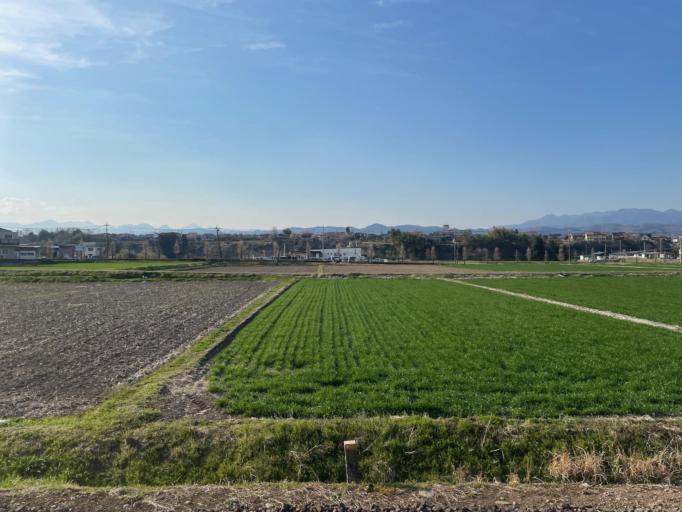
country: JP
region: Gunma
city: Annaka
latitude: 36.3169
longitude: 138.8894
